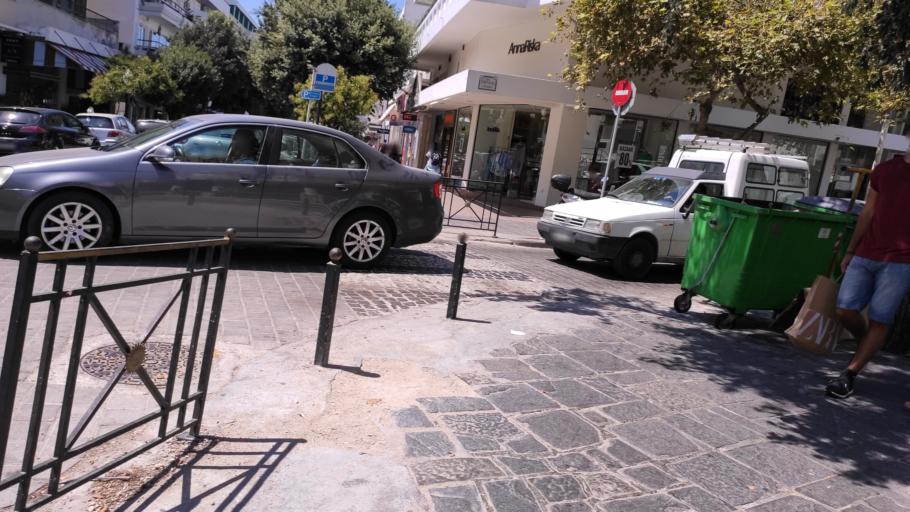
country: GR
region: South Aegean
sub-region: Nomos Dodekanisou
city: Rodos
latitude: 36.4487
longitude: 28.2229
